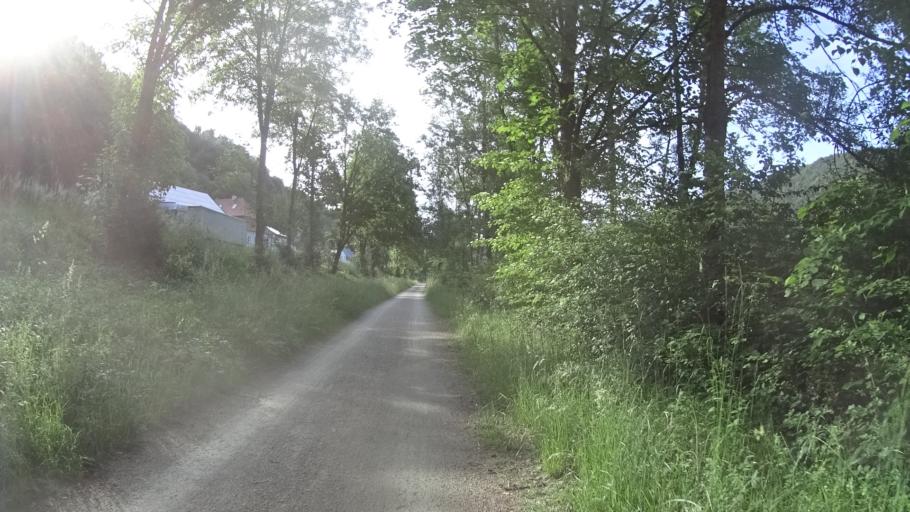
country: DE
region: Bavaria
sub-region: Lower Bavaria
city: Riedenburg
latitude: 48.9491
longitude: 11.7386
